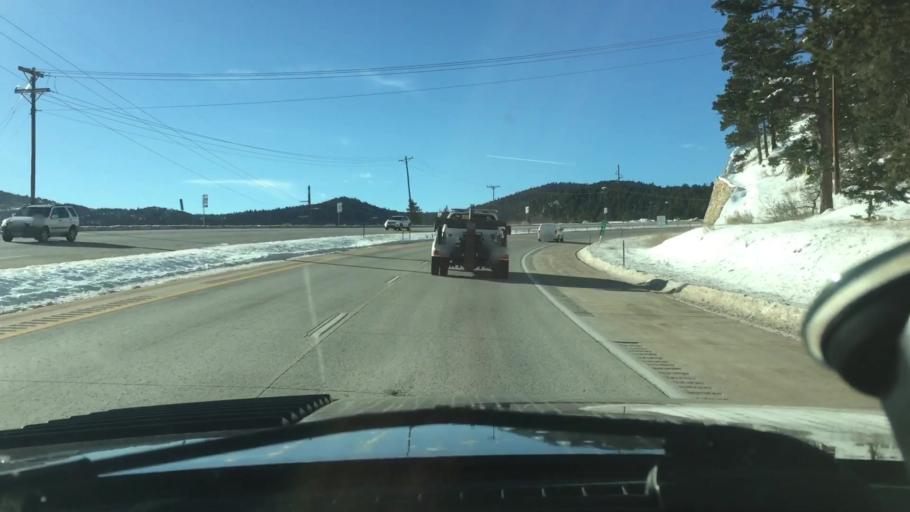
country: US
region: Colorado
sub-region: Jefferson County
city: Indian Hills
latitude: 39.5552
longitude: -105.2402
